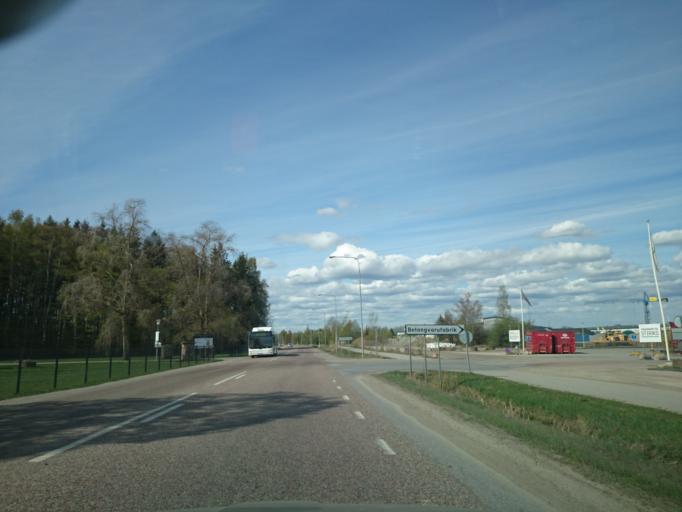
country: SE
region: Uppsala
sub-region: Uppsala Kommun
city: Gamla Uppsala
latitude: 59.8741
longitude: 17.5949
